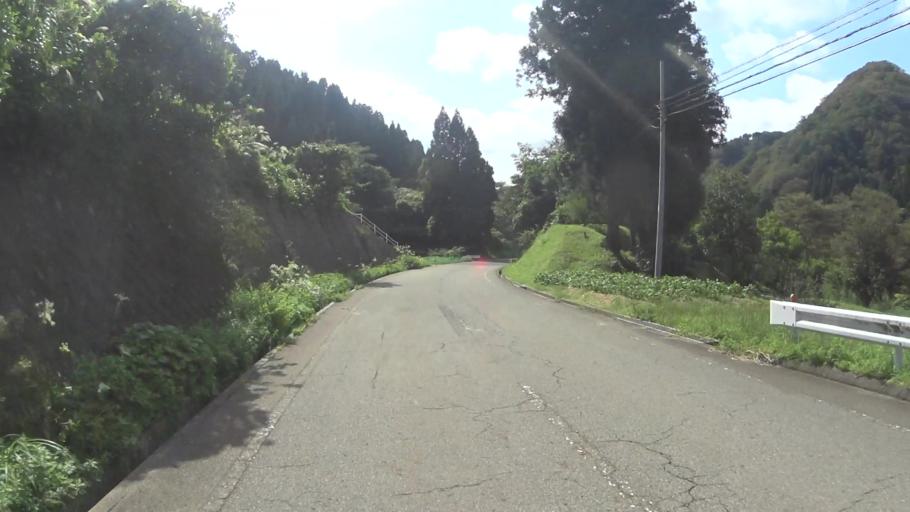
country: JP
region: Kyoto
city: Miyazu
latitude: 35.6971
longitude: 135.1760
